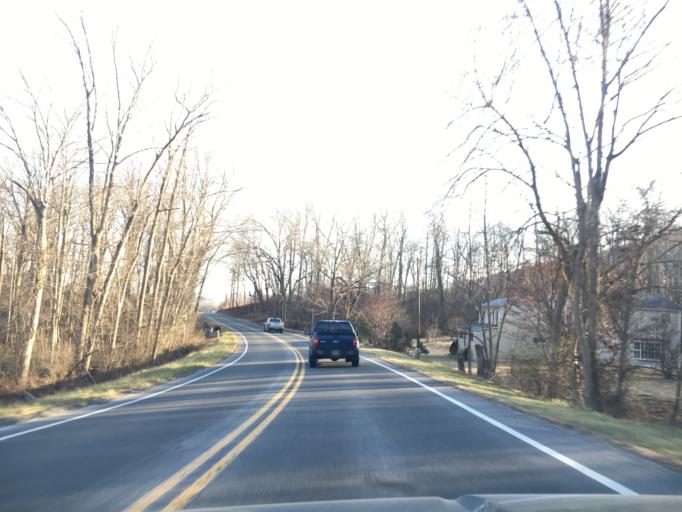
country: US
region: Virginia
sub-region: Warren County
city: Apple Mountain Lake
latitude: 38.8433
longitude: -78.1252
